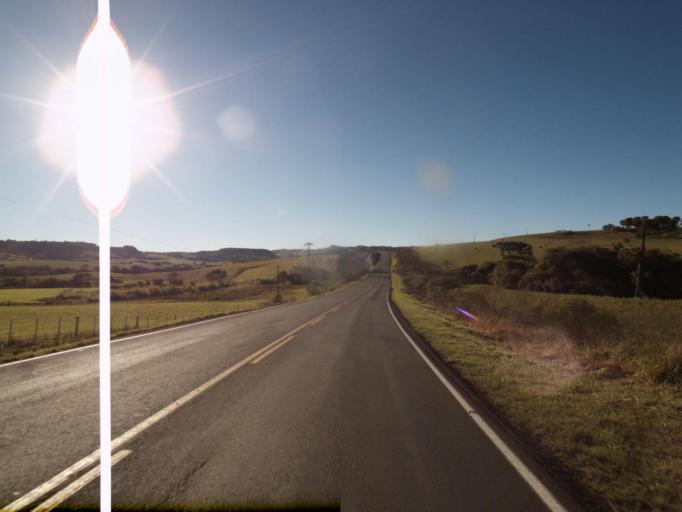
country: AR
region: Misiones
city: Bernardo de Irigoyen
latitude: -26.3542
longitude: -53.5436
